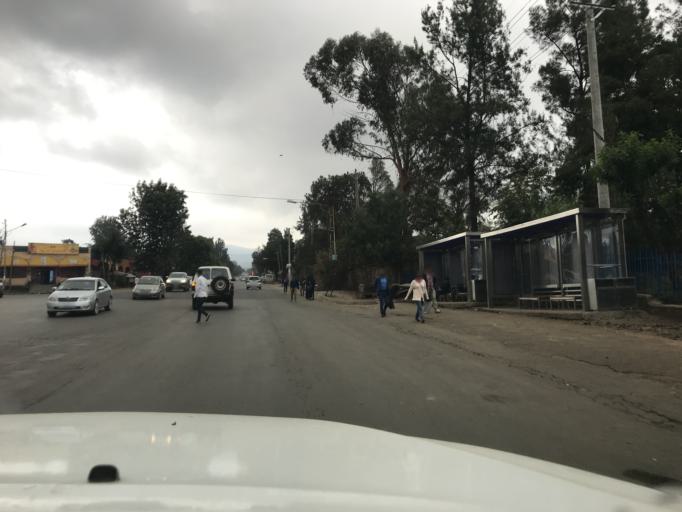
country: ET
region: Adis Abeba
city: Addis Ababa
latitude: 9.0473
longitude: 38.7617
